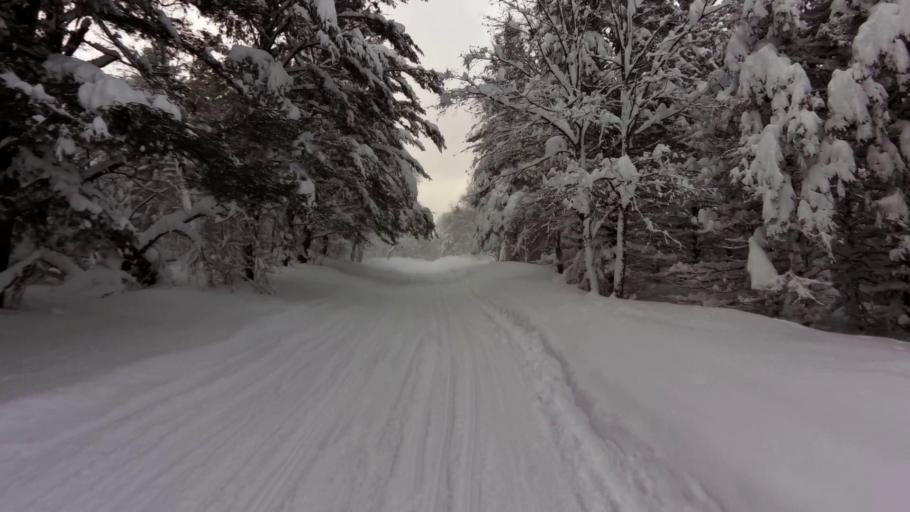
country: US
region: New York
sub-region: Lewis County
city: Lowville
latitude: 43.7425
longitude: -75.6734
